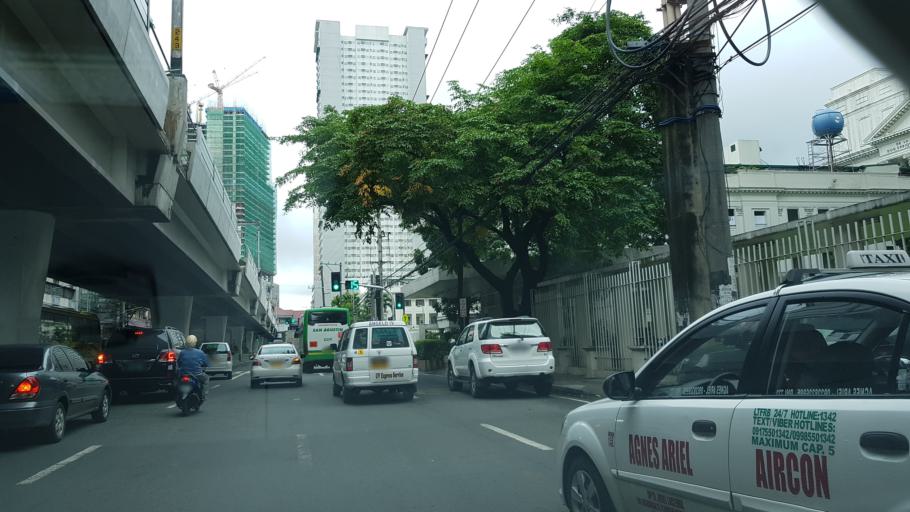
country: PH
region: Metro Manila
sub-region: City of Manila
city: Port Area
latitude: 14.5655
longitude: 120.9938
